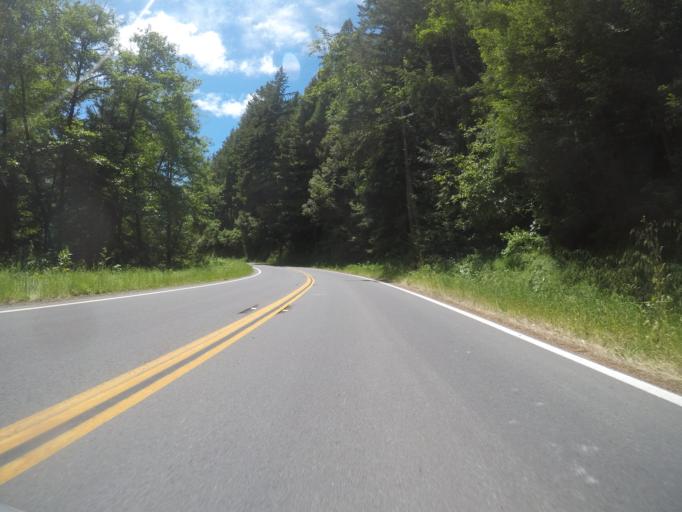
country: US
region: California
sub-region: Del Norte County
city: Bertsch-Oceanview
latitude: 41.5233
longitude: -124.0181
